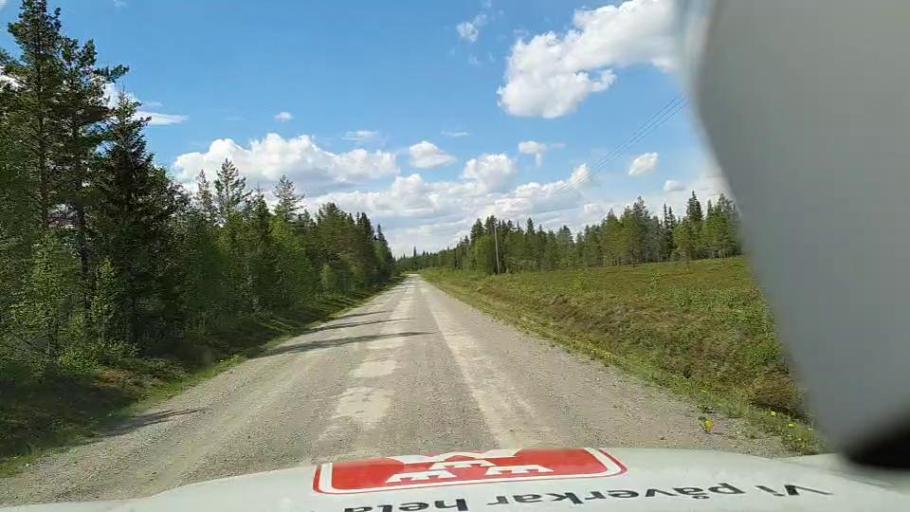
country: SE
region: Vaesterbotten
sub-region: Vilhelmina Kommun
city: Sjoberg
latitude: 64.5434
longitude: 15.6505
